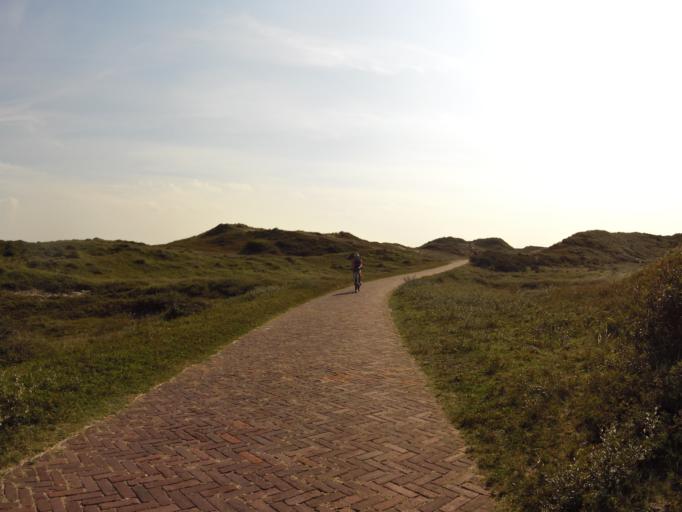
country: NL
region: North Holland
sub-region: Gemeente Bergen
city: Egmond aan Zee
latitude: 52.6534
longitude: 4.6313
